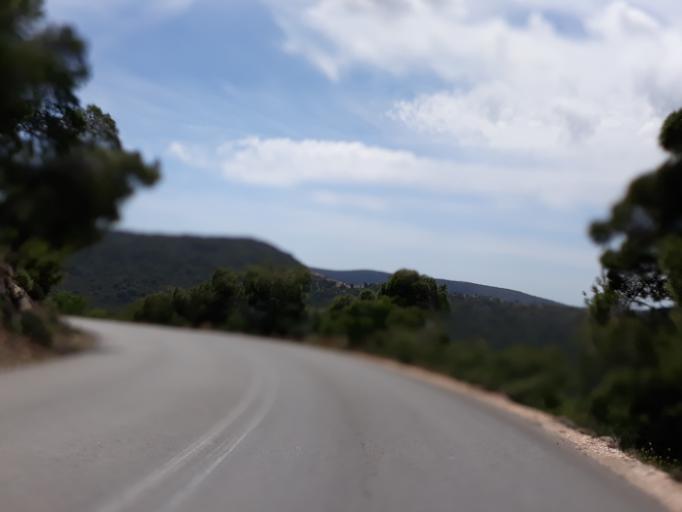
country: GR
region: Attica
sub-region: Nomarchia Dytikis Attikis
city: Magoula
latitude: 38.1482
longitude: 23.5174
